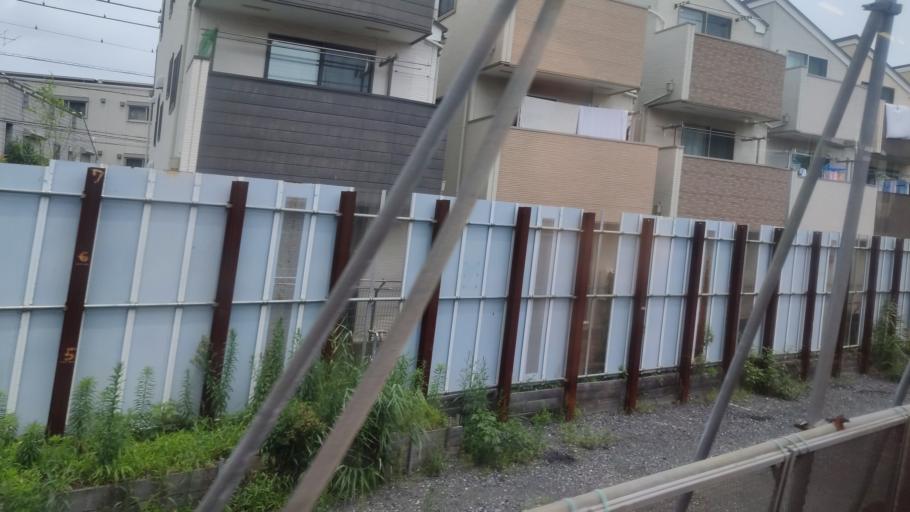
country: JP
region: Chiba
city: Matsudo
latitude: 35.7367
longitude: 139.8418
